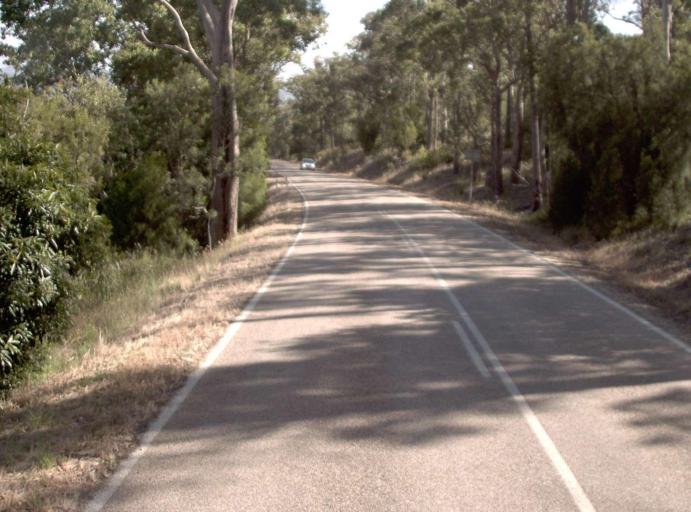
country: AU
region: Victoria
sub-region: East Gippsland
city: Lakes Entrance
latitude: -37.7611
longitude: 147.8133
